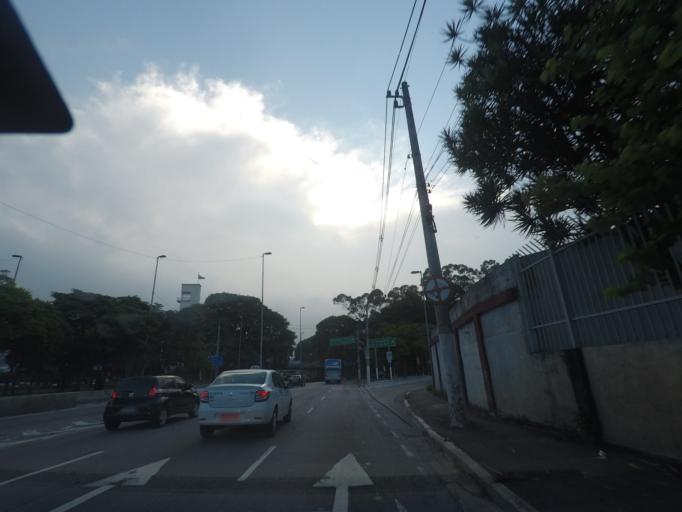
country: BR
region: Sao Paulo
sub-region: Sao Paulo
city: Sao Paulo
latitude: -23.5197
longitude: -46.6318
